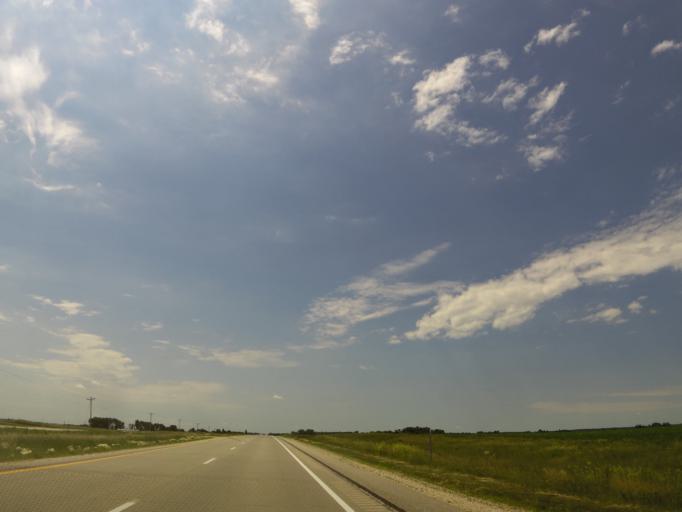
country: US
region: Iowa
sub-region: Bremer County
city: Denver
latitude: 42.7396
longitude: -92.3377
